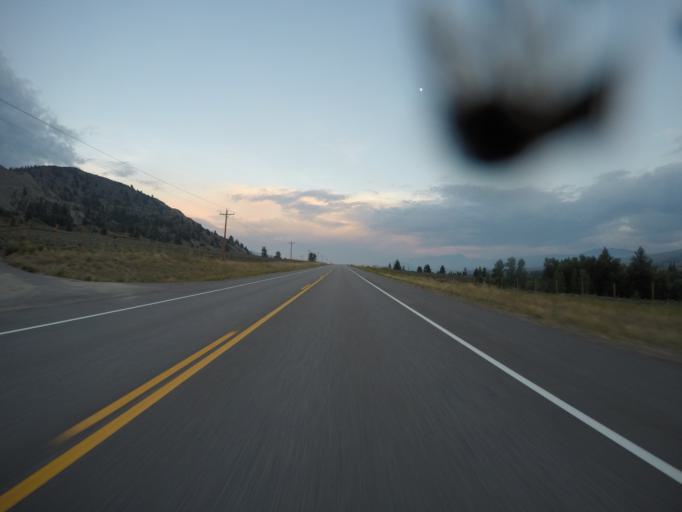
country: US
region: Colorado
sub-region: Grand County
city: Kremmling
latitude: 39.9958
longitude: -106.3643
